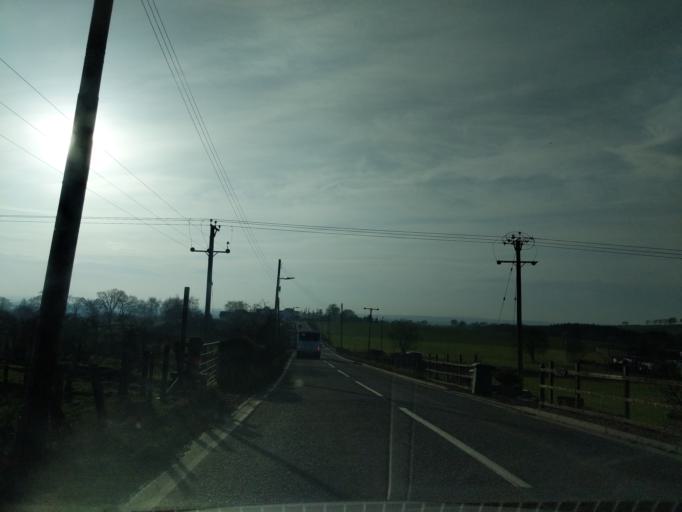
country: GB
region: Scotland
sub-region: South Lanarkshire
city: Law
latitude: 55.7376
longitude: -3.8594
